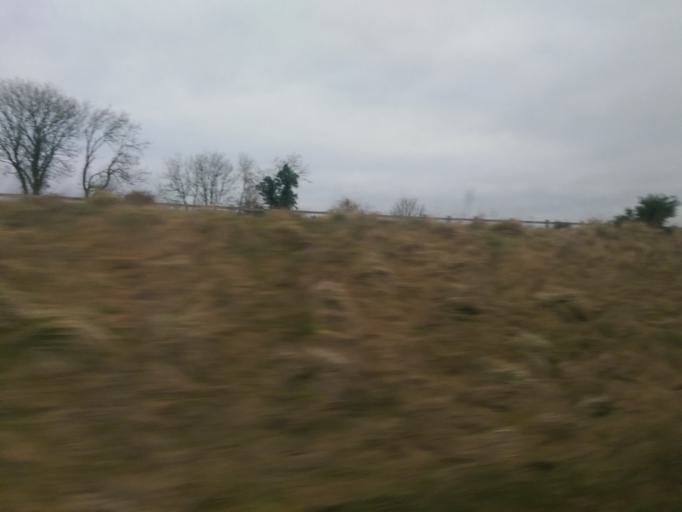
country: IE
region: Connaught
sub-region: County Galway
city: Ballinasloe
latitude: 53.3166
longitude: -8.1633
